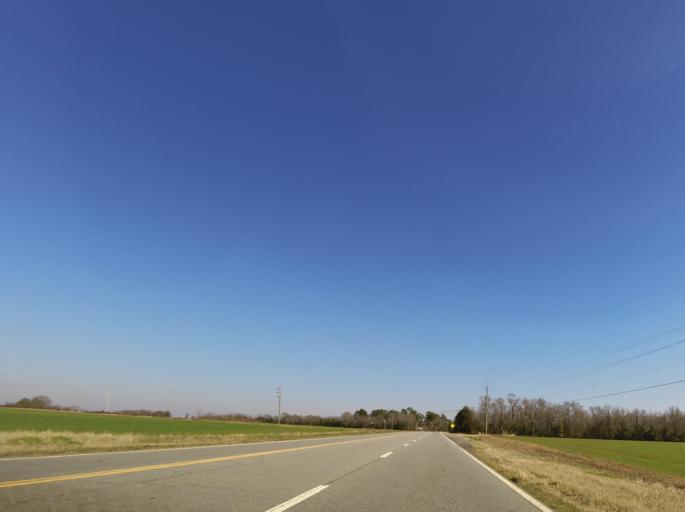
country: US
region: Georgia
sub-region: Bleckley County
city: Cochran
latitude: 32.3544
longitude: -83.3916
